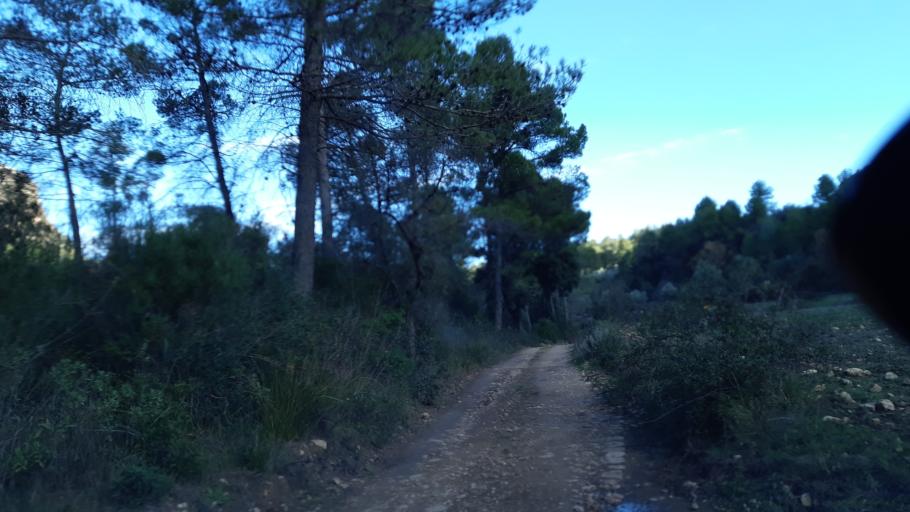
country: ES
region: Aragon
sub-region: Provincia de Teruel
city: Lledo
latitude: 40.8649
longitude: 0.2538
